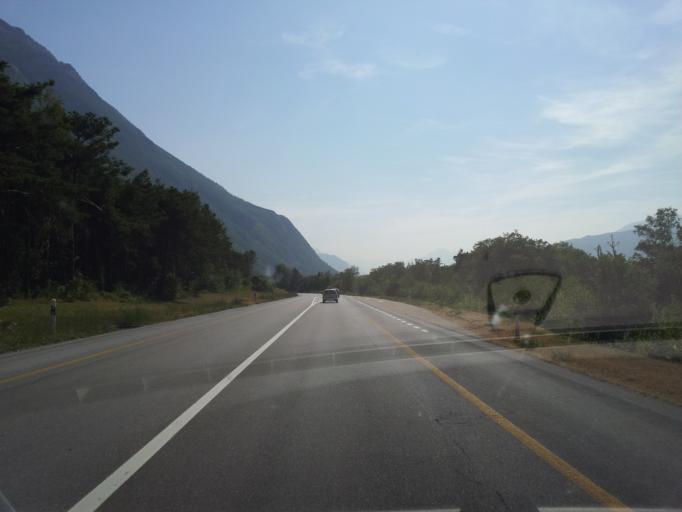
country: CH
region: Valais
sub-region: Leuk District
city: Varen
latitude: 46.3075
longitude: 7.6131
